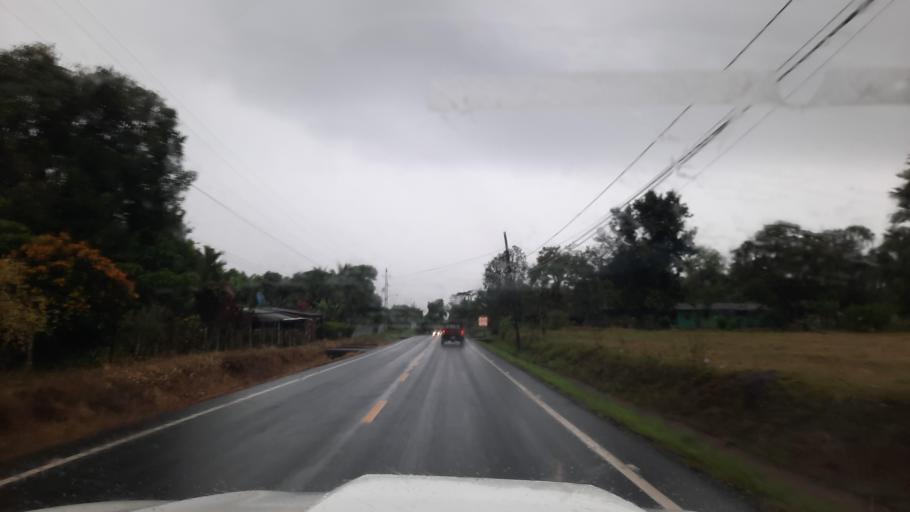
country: PA
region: Chiriqui
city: Sortova
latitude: 8.5478
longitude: -82.6252
